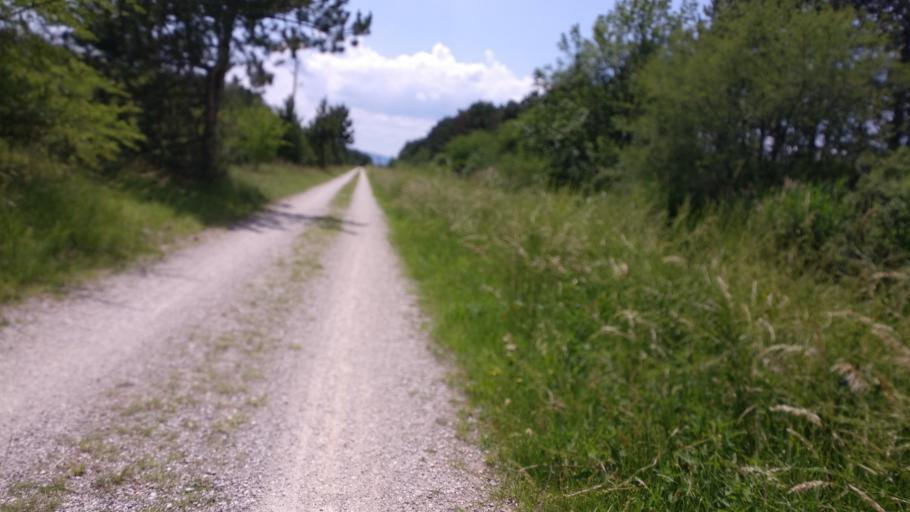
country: AT
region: Lower Austria
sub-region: Politischer Bezirk Wiener Neustadt
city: Lichtenworth
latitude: 47.8630
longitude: 16.2816
